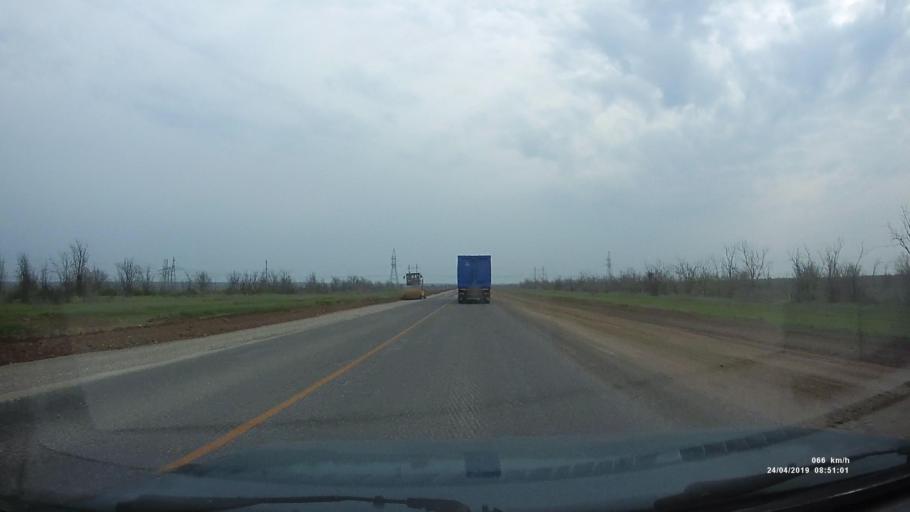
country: RU
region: Kalmykiya
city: Arshan'
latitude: 46.2648
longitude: 44.1446
